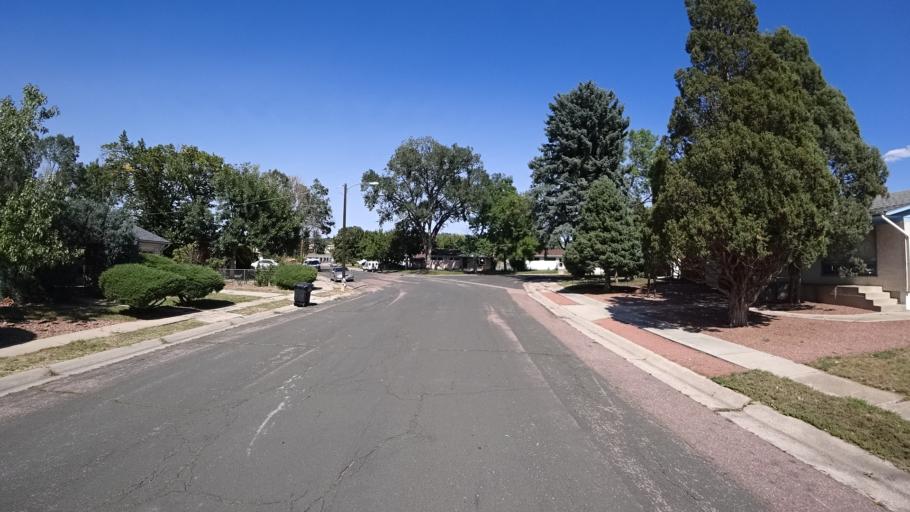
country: US
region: Colorado
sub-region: El Paso County
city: Colorado Springs
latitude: 38.8833
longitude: -104.8083
